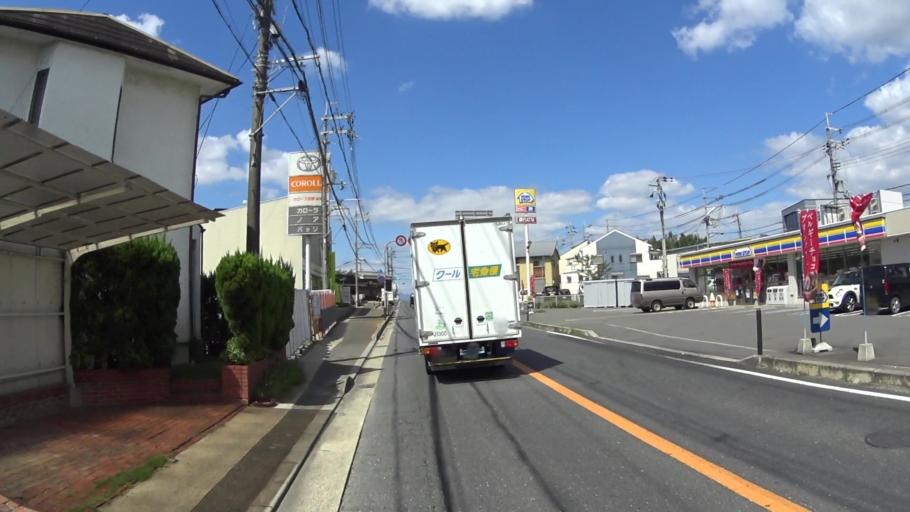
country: JP
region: Kyoto
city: Tanabe
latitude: 34.8491
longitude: 135.7841
